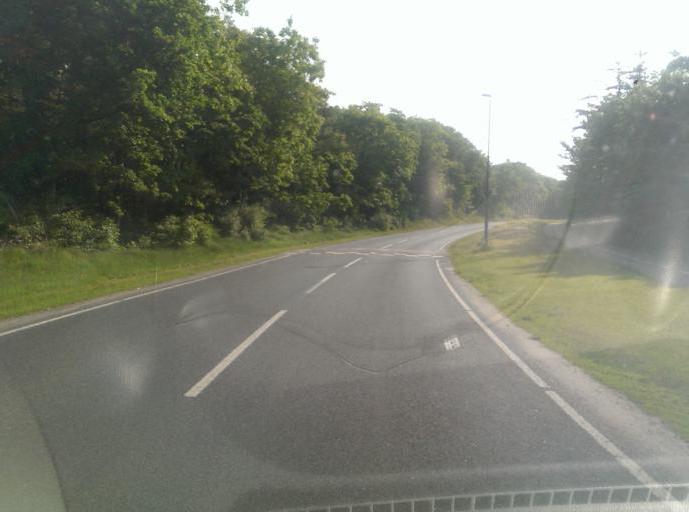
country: DK
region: South Denmark
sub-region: Esbjerg Kommune
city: Bramming
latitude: 55.4281
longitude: 8.6564
